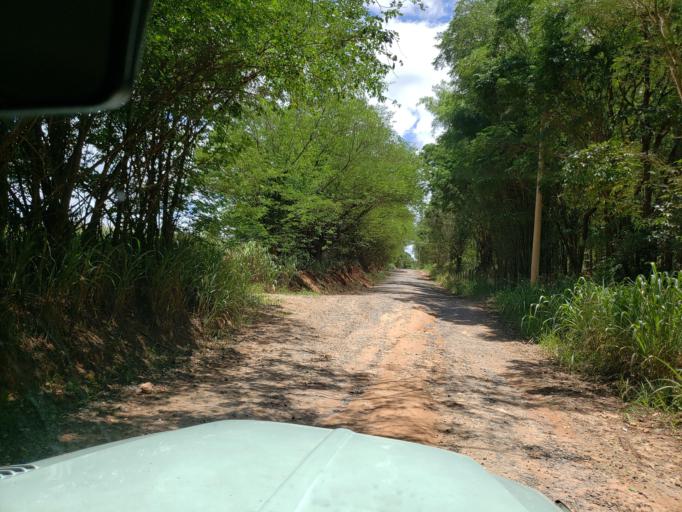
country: BR
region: Sao Paulo
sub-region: Moji-Guacu
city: Mogi-Gaucu
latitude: -22.2561
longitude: -46.8489
